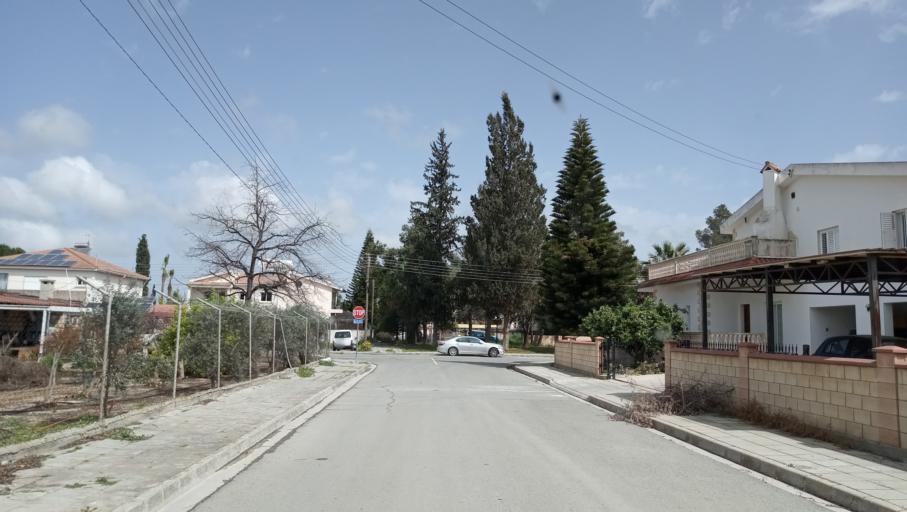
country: CY
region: Lefkosia
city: Dali
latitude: 35.0214
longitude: 33.4253
